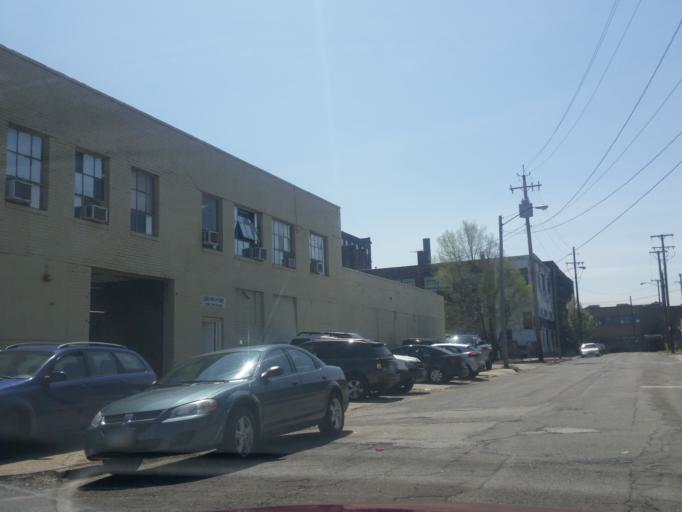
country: US
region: Ohio
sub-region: Cuyahoga County
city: Cleveland
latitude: 41.5098
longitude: -81.6605
